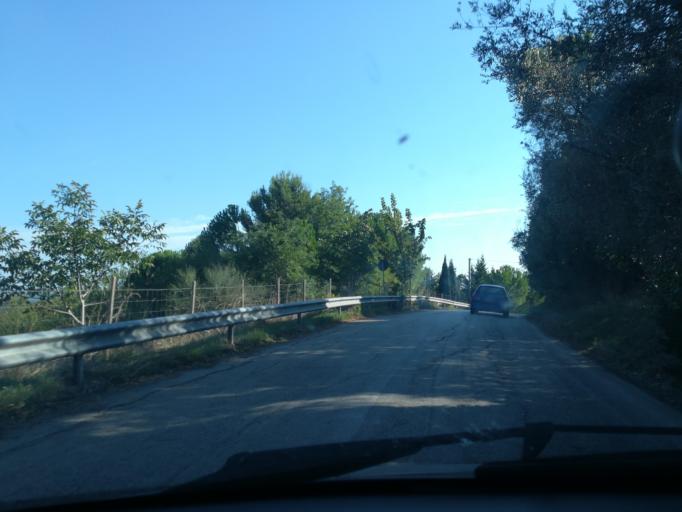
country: IT
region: The Marches
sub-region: Provincia di Macerata
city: Piediripa
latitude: 43.2908
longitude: 13.4887
